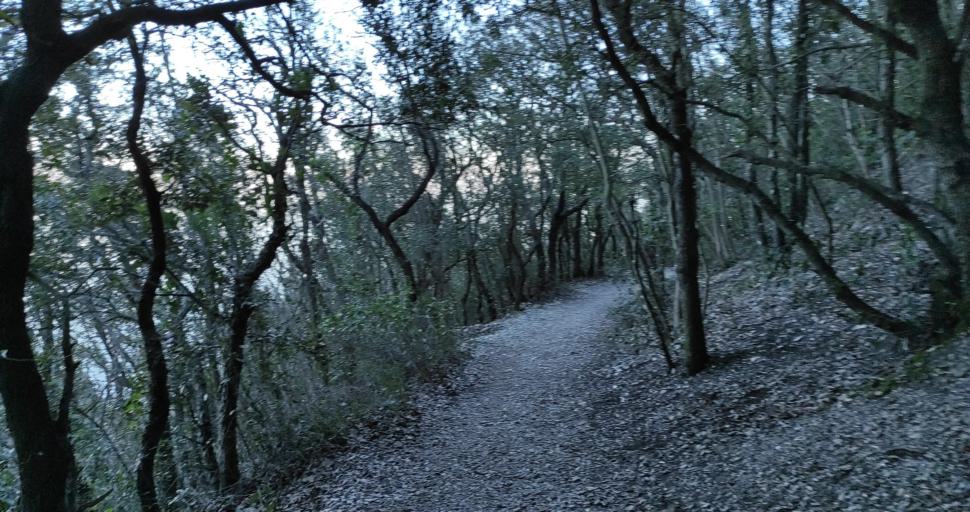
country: IT
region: The Marches
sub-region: Provincia di Ancona
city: Sirolo
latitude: 43.5467
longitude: 13.6196
